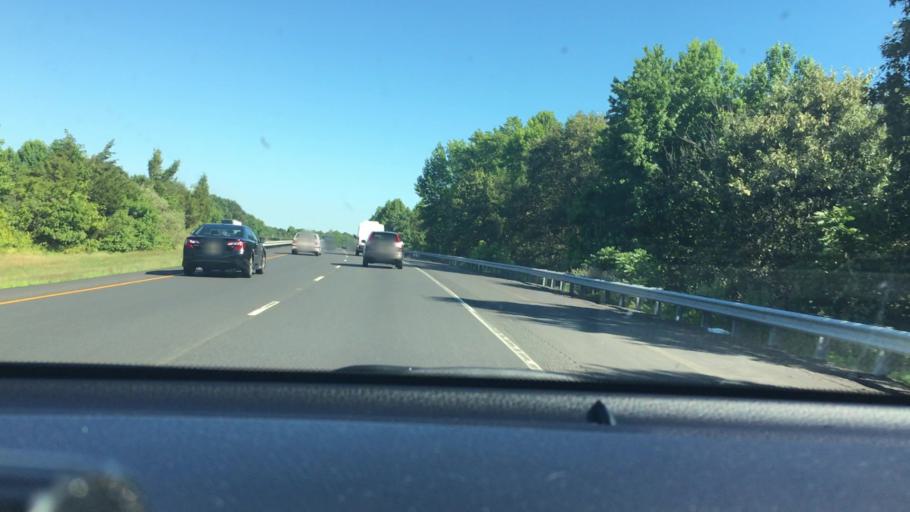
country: US
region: New Jersey
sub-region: Gloucester County
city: Clayton
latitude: 39.6213
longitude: -75.0897
